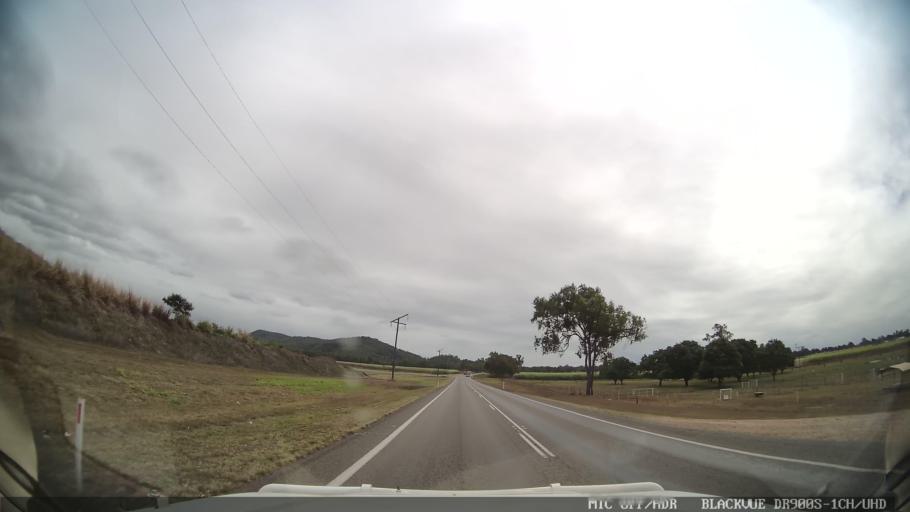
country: AU
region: Queensland
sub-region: Hinchinbrook
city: Ingham
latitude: -18.8568
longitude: 146.1644
